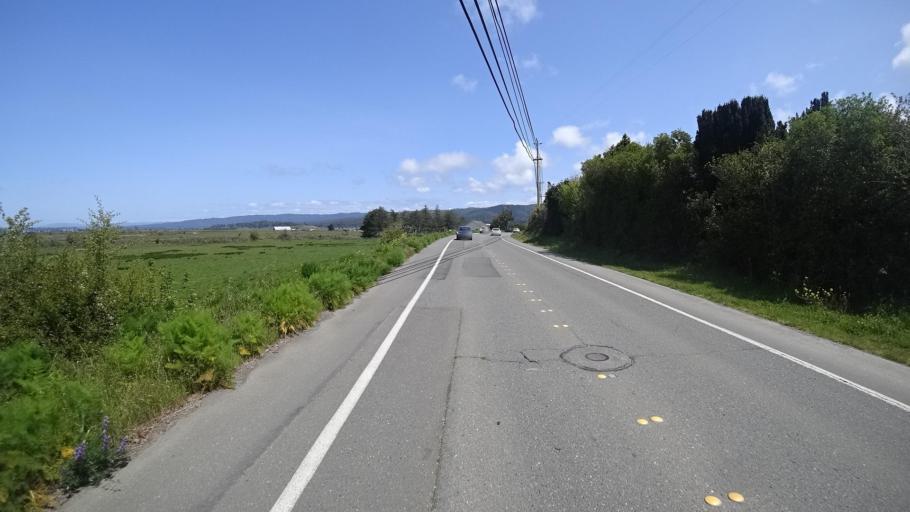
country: US
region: California
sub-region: Humboldt County
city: Myrtletown
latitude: 40.7862
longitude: -124.1151
